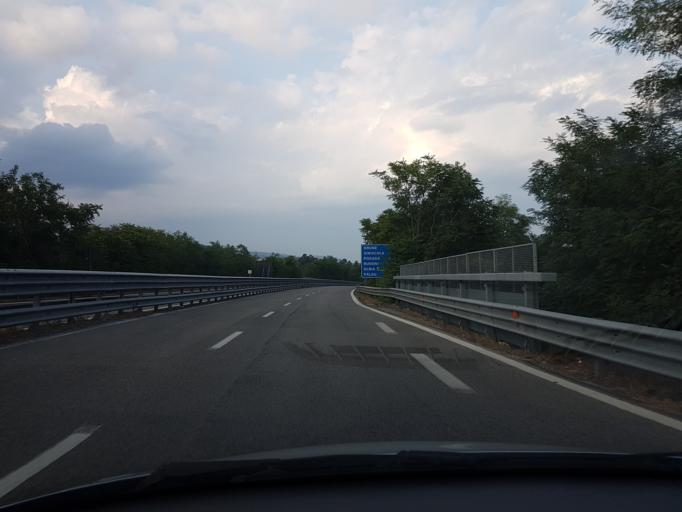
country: IT
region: Sardinia
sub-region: Provincia di Nuoro
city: Nuoro
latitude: 40.3247
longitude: 9.2817
